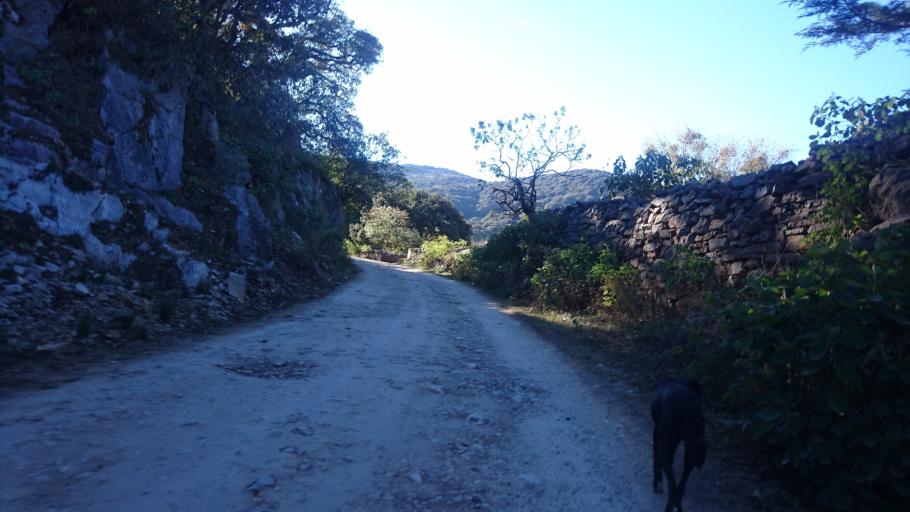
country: MX
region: San Luis Potosi
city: Zaragoza
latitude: 22.0312
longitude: -100.6099
